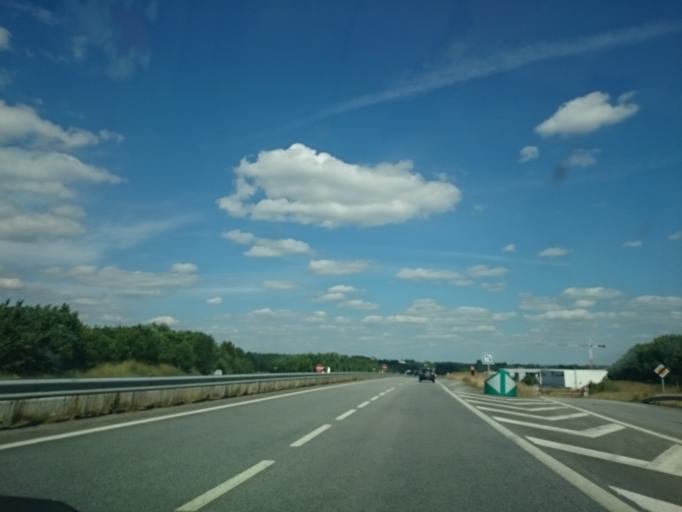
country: FR
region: Brittany
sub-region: Departement des Cotes-d'Armor
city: Saint-Barnabe
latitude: 48.1809
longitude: -2.6918
